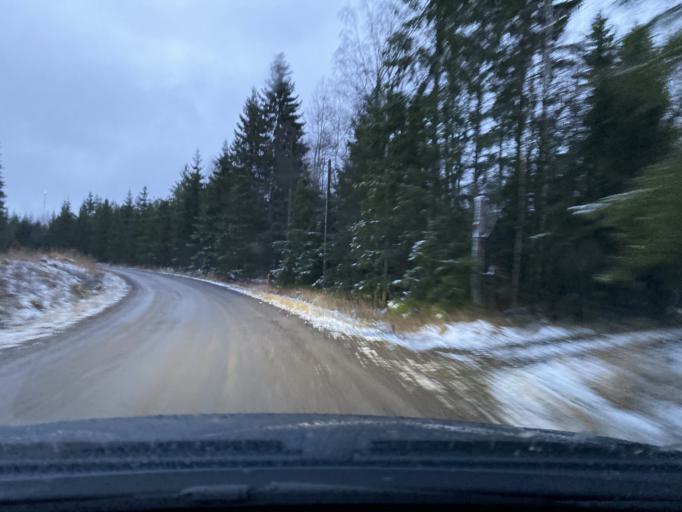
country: FI
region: Pirkanmaa
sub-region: Lounais-Pirkanmaa
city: Punkalaidun
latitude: 61.1464
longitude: 22.9510
